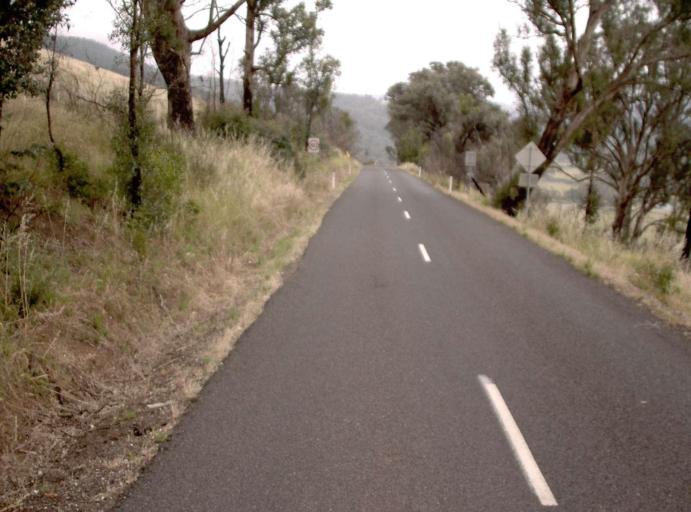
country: AU
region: Victoria
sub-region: Wellington
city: Heyfield
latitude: -37.8218
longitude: 146.6754
